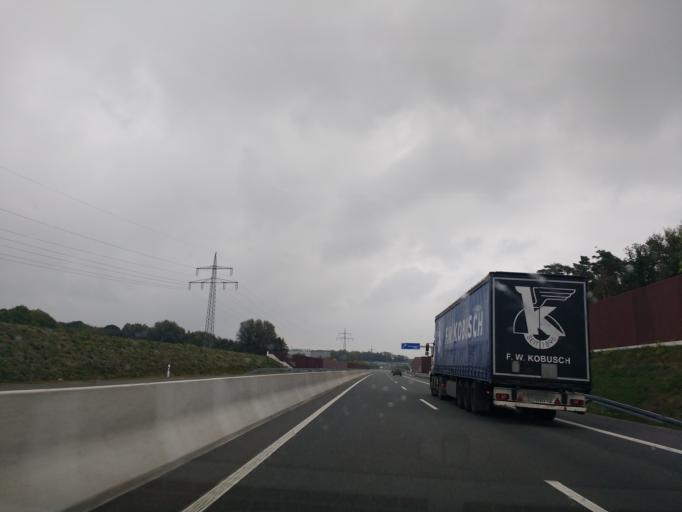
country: DE
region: North Rhine-Westphalia
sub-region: Regierungsbezirk Detmold
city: Steinhagen
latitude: 52.0109
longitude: 8.4211
